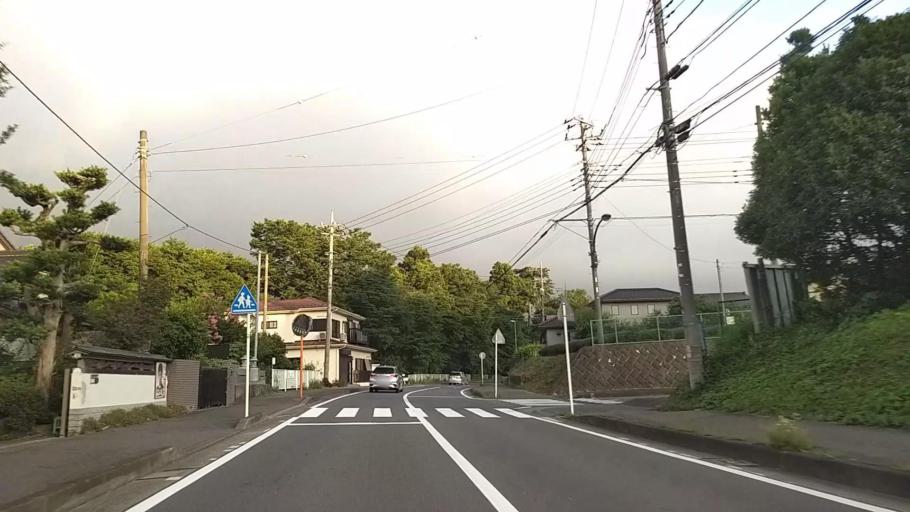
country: JP
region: Kanagawa
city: Atsugi
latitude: 35.4751
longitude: 139.2842
